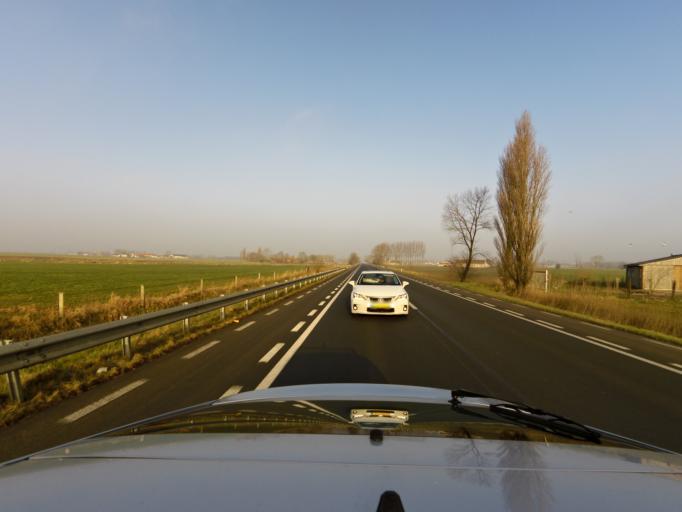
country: BE
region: Flanders
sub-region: Provincie West-Vlaanderen
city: Gistel
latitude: 51.1395
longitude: 2.9702
